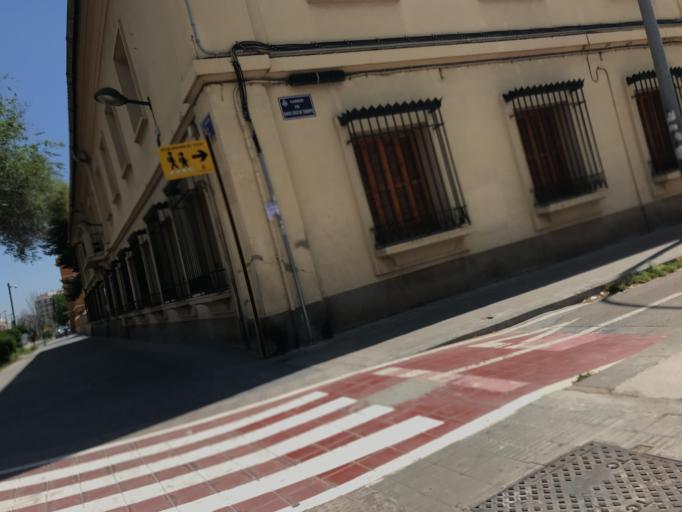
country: ES
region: Valencia
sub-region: Provincia de Valencia
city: Mislata
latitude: 39.4685
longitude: -0.3997
